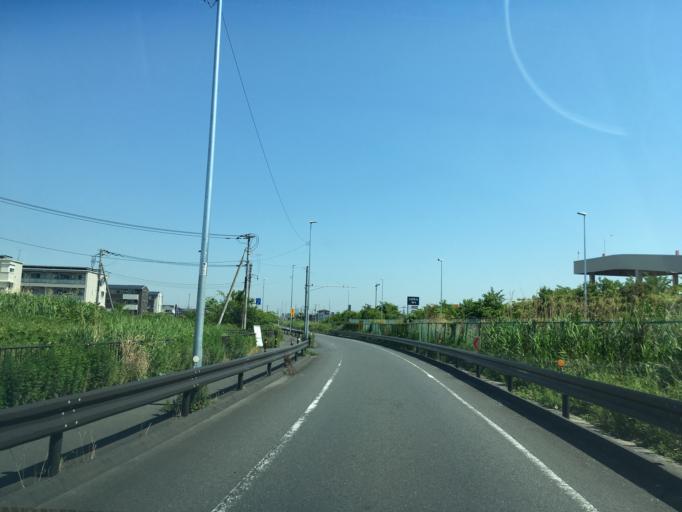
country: JP
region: Saitama
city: Yoshikawa
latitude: 35.8829
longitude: 139.8263
